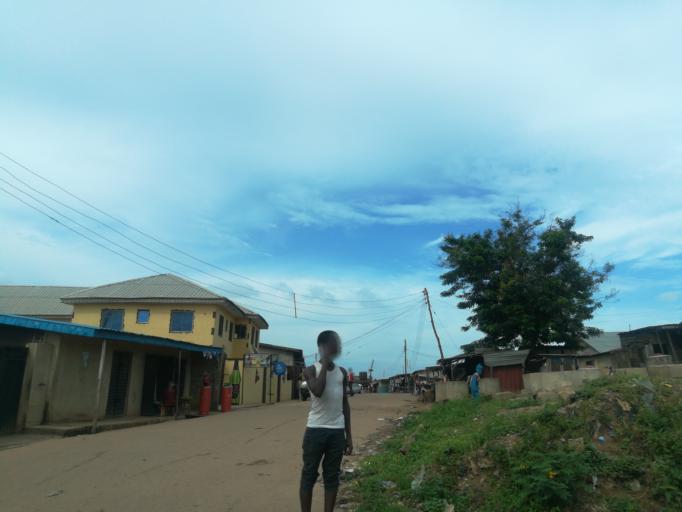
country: NG
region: Oyo
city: Ibadan
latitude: 7.3824
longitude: 3.9434
